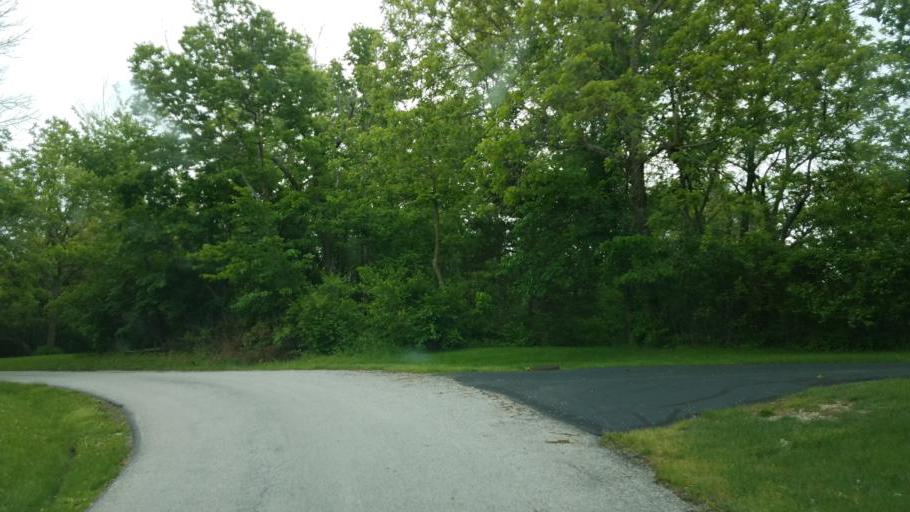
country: US
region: Iowa
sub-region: Decatur County
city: Lamoni
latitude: 40.6207
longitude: -93.9271
